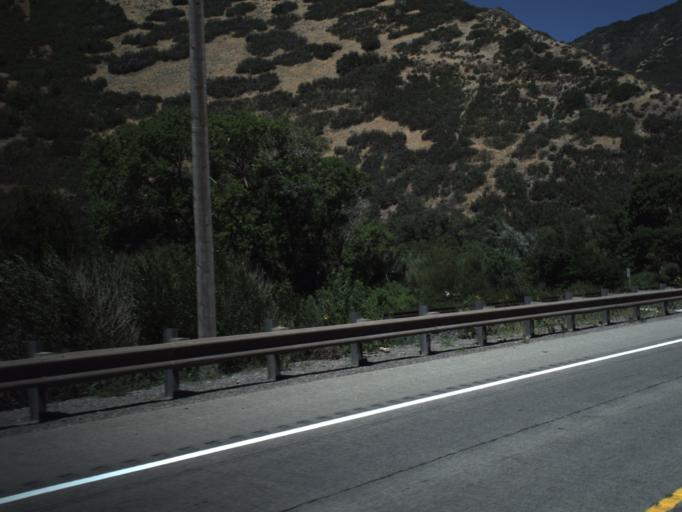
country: US
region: Utah
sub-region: Utah County
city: Mapleton
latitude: 40.0474
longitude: -111.5482
